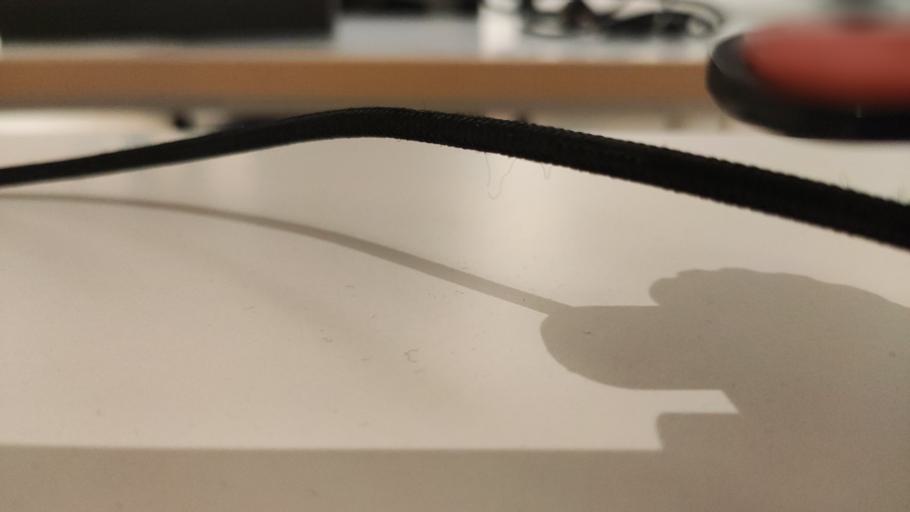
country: RU
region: Kaluga
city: Borovsk
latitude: 55.3715
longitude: 36.4106
